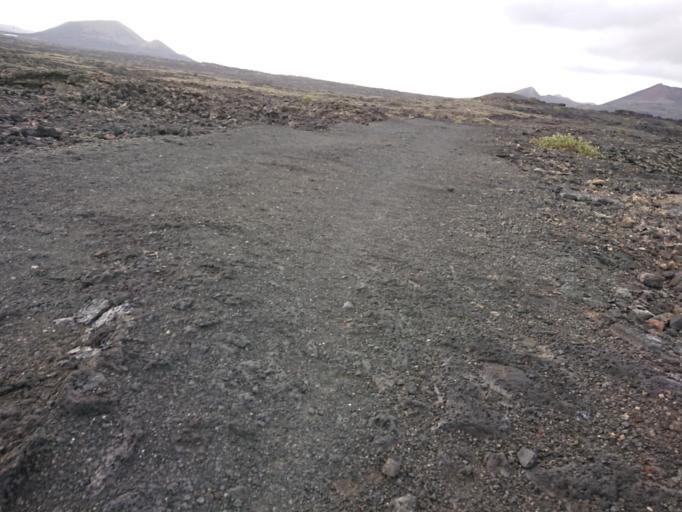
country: ES
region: Canary Islands
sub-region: Provincia de Las Palmas
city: Tias
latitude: 29.0011
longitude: -13.6898
